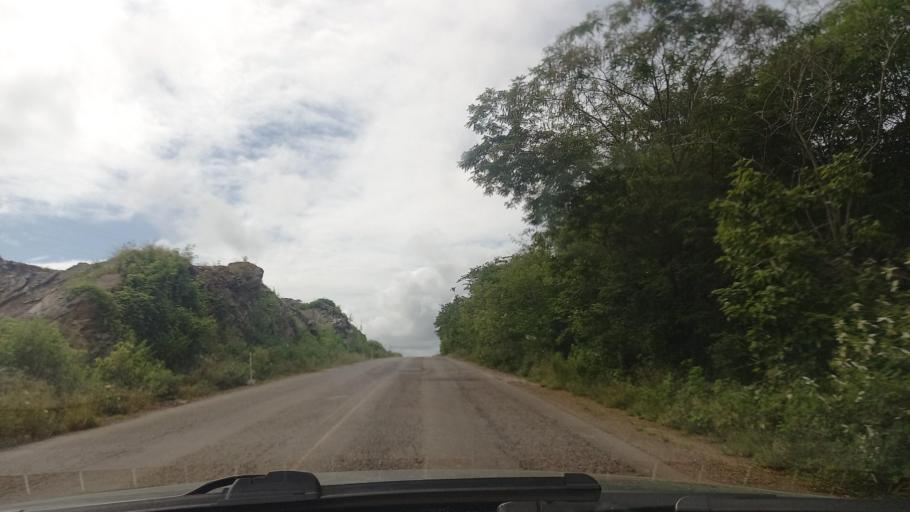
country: BR
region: Alagoas
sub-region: Batalha
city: Batalha
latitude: -9.6646
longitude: -37.1627
